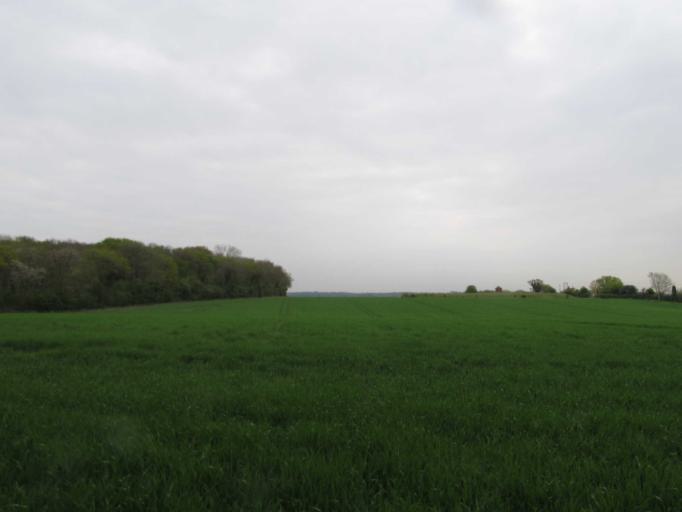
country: GB
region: England
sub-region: Royal Borough of Windsor and Maidenhead
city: Bisham
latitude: 51.5421
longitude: -0.7539
